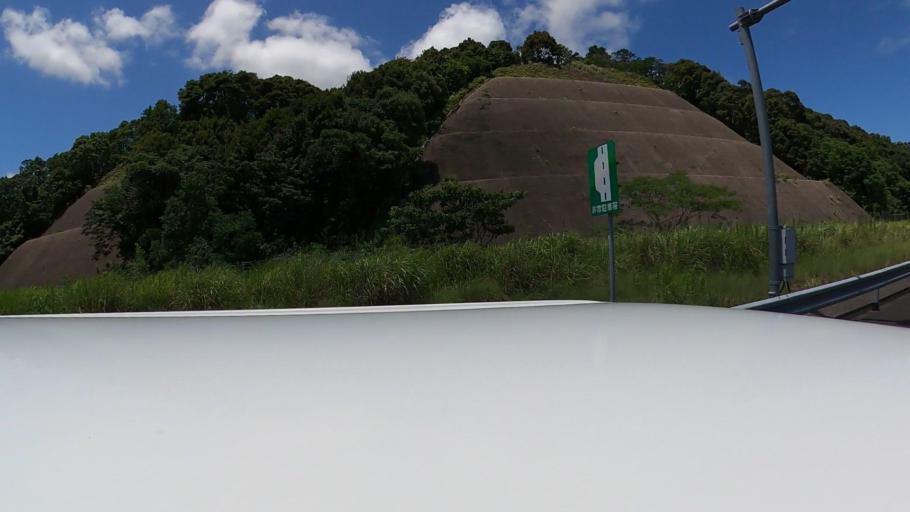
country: JP
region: Miyazaki
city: Nobeoka
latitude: 32.4969
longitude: 131.6595
